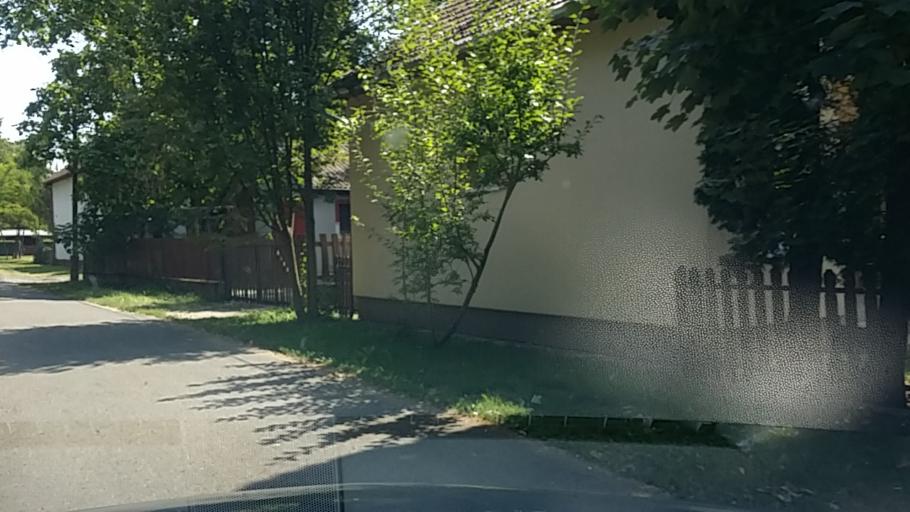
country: HU
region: Bekes
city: Gyomaendrod
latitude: 46.9357
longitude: 20.8370
